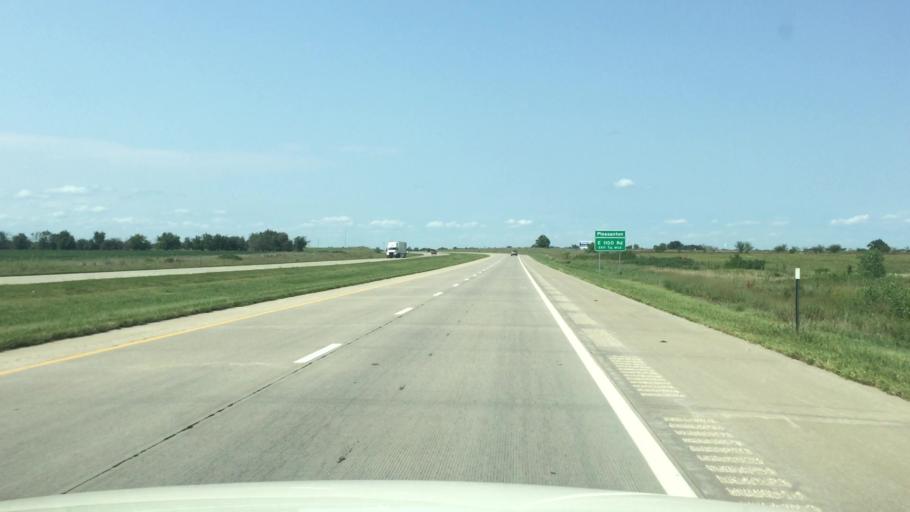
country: US
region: Kansas
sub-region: Linn County
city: Pleasanton
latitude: 38.1688
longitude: -94.6957
